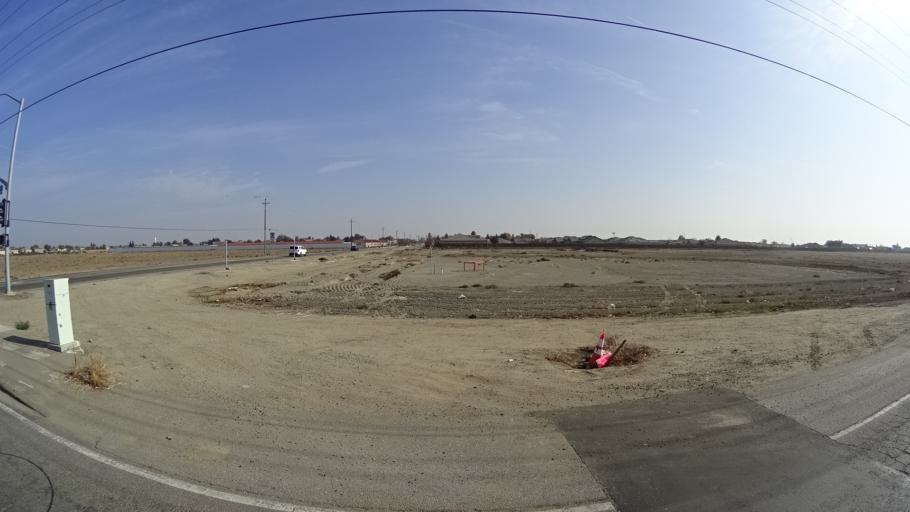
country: US
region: California
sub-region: Kern County
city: Greenacres
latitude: 35.2959
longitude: -119.1099
